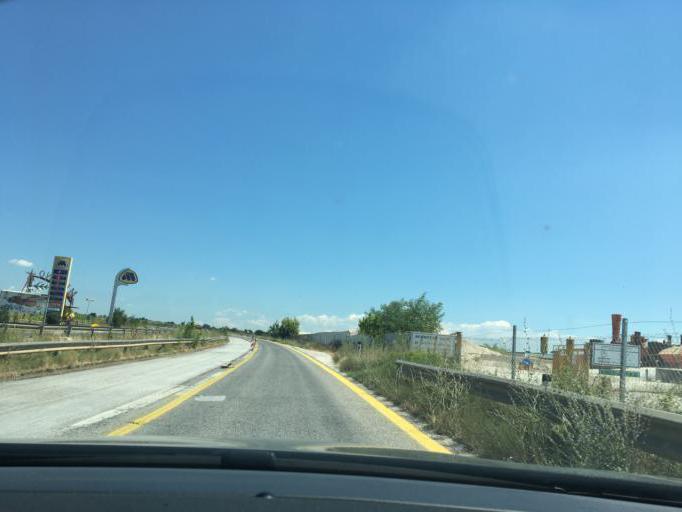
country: MK
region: Kumanovo
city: Romanovce
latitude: 42.0768
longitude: 21.7000
